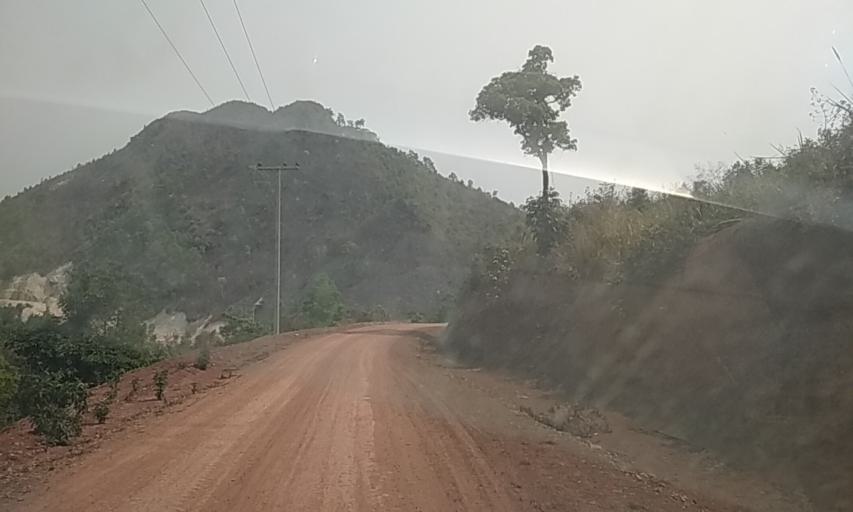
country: VN
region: Huyen Dien Bien
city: Dien Bien Phu
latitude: 21.4780
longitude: 102.7780
